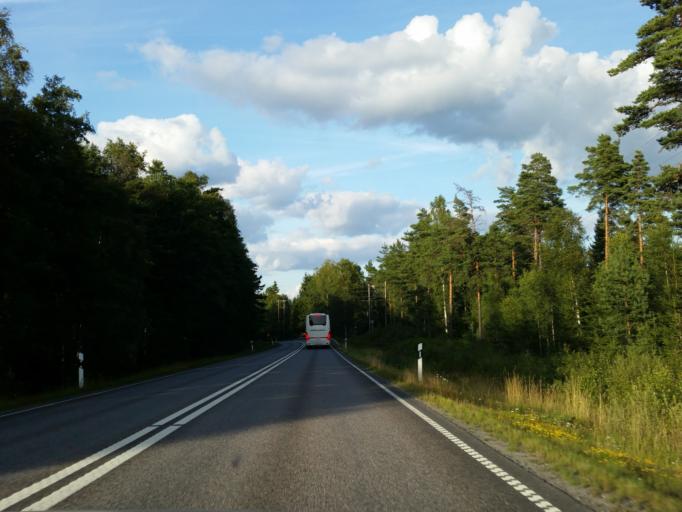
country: SE
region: Stockholm
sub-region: Sodertalje Kommun
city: Molnbo
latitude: 59.0695
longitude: 17.5328
